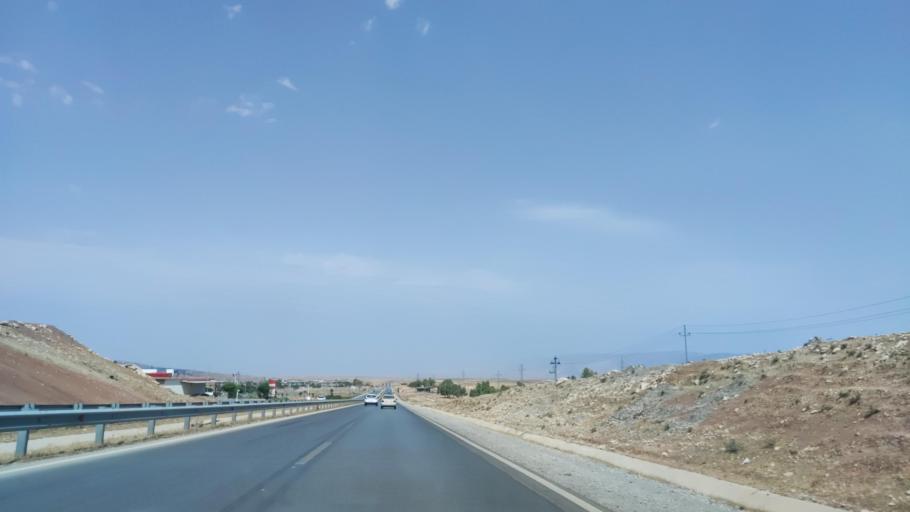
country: IQ
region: Arbil
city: Shaqlawah
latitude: 36.4953
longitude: 44.3665
